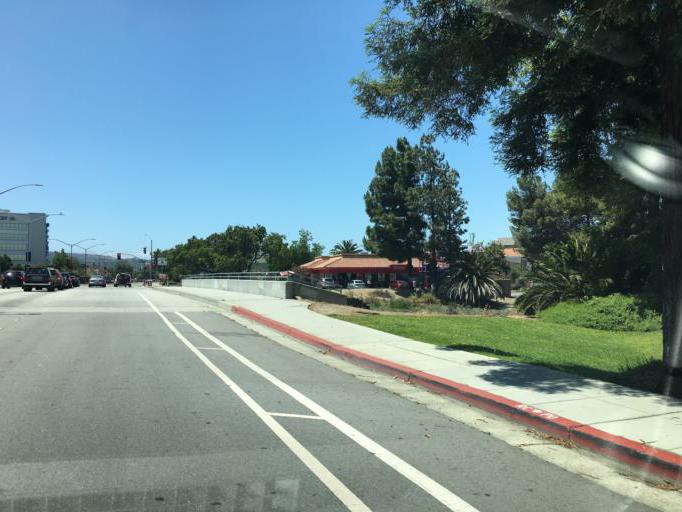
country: US
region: California
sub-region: San Mateo County
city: Redwood City
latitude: 37.4900
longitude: -122.2253
